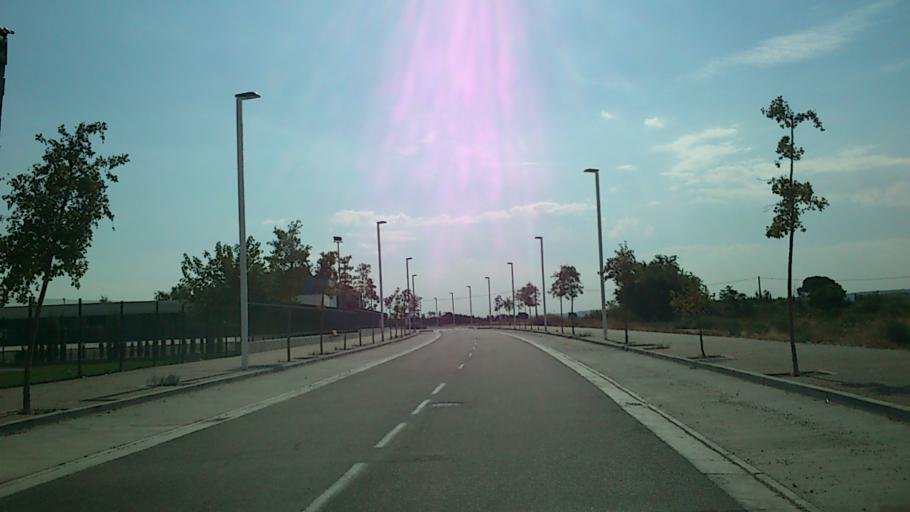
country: ES
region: Aragon
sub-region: Provincia de Zaragoza
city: Puebla de Alfinden
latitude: 41.6316
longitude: -0.7583
